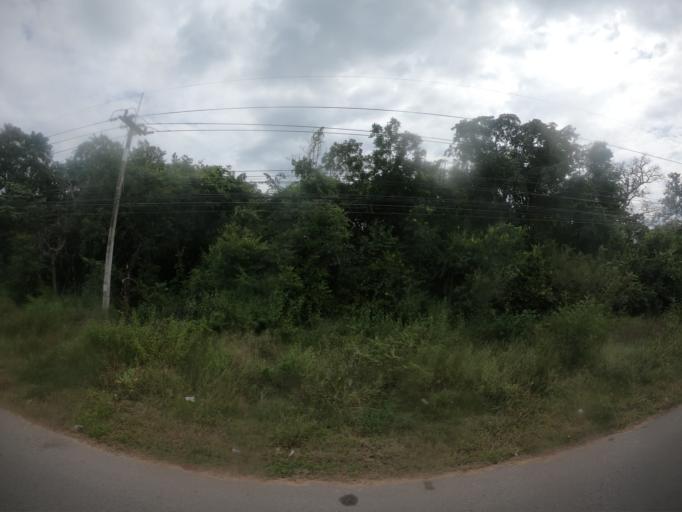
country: TH
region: Maha Sarakham
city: Kantharawichai
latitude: 16.2825
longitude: 103.2920
